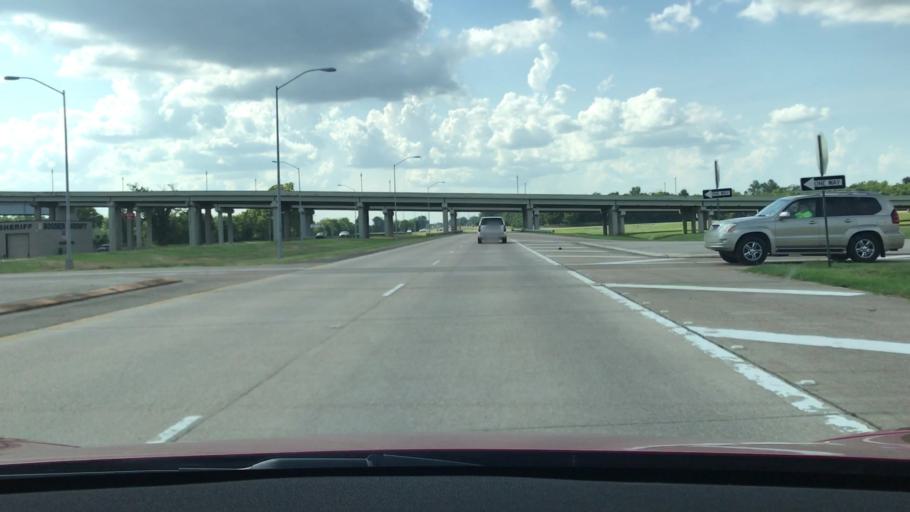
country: US
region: Louisiana
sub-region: Bossier Parish
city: Bossier City
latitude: 32.4931
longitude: -93.6948
